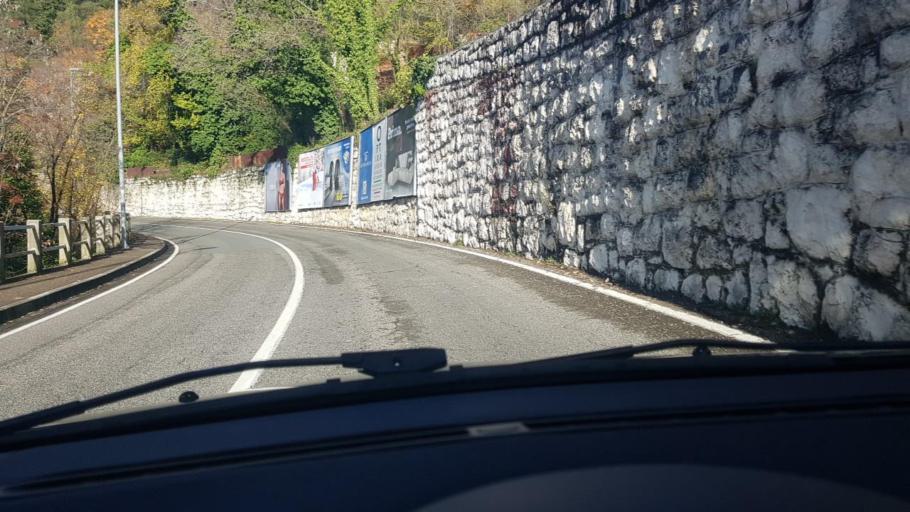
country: HR
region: Primorsko-Goranska
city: Matulji
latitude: 45.3555
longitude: 14.3326
